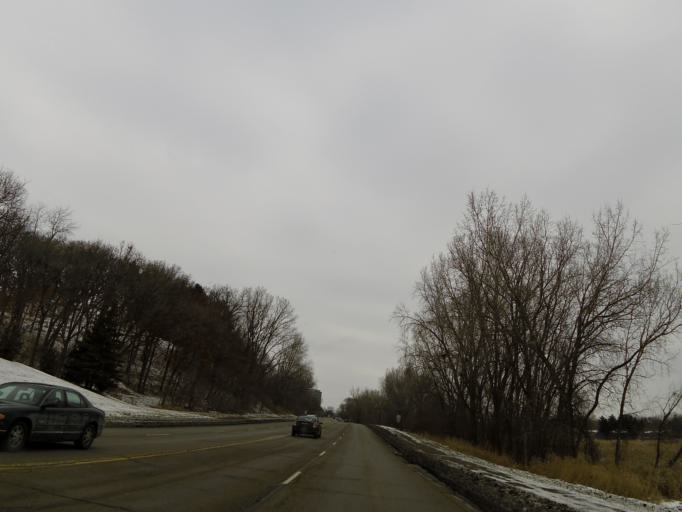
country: US
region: Minnesota
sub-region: Hennepin County
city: Edina
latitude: 44.8433
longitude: -93.3500
